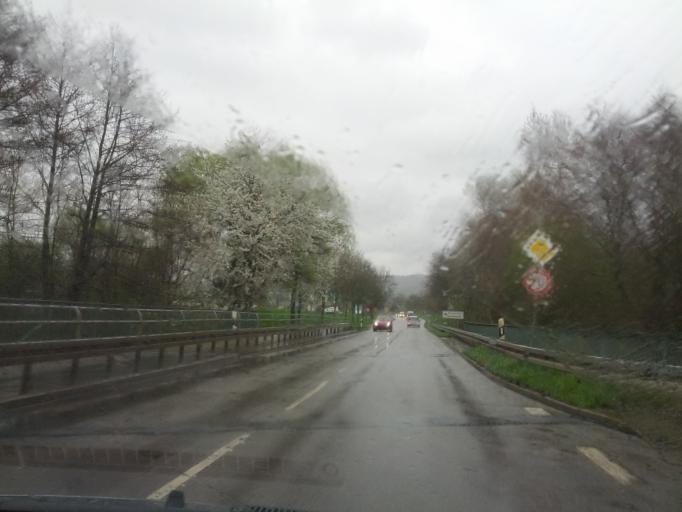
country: DE
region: Baden-Wuerttemberg
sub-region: Freiburg Region
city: Bad Krozingen
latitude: 47.9188
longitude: 7.7251
